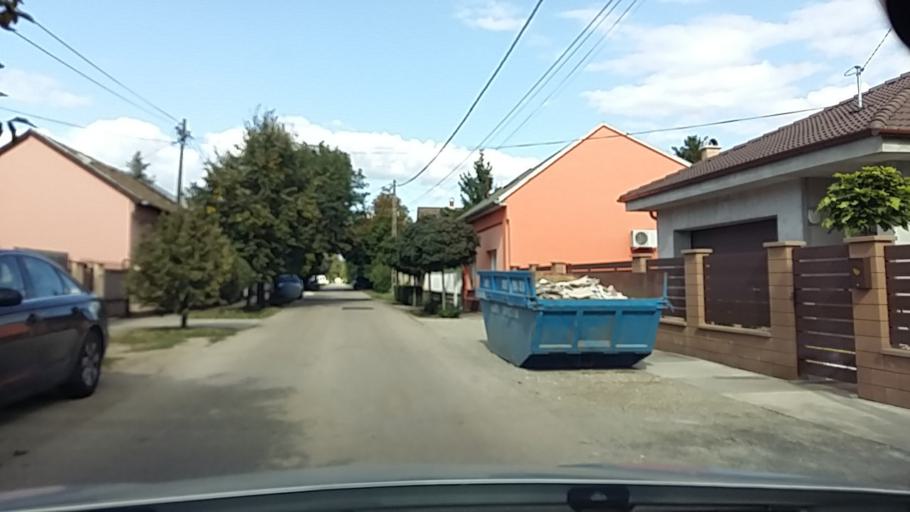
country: HU
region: Pest
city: Vecses
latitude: 47.4070
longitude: 19.2610
